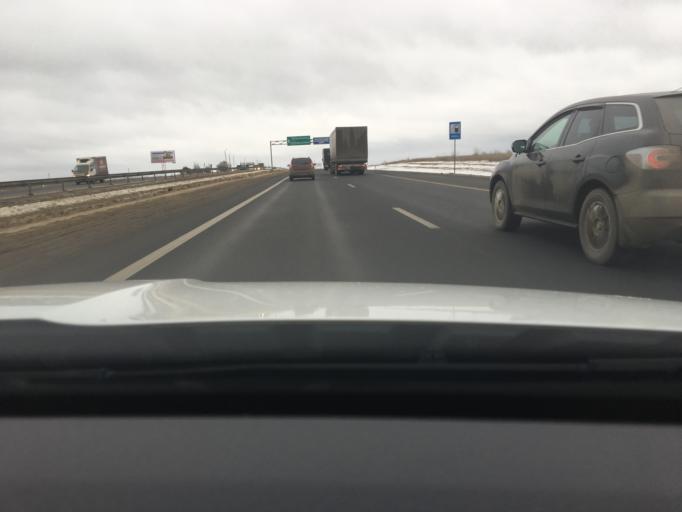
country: RU
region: Moskovskaya
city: Serpukhov
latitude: 54.8436
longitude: 37.4645
